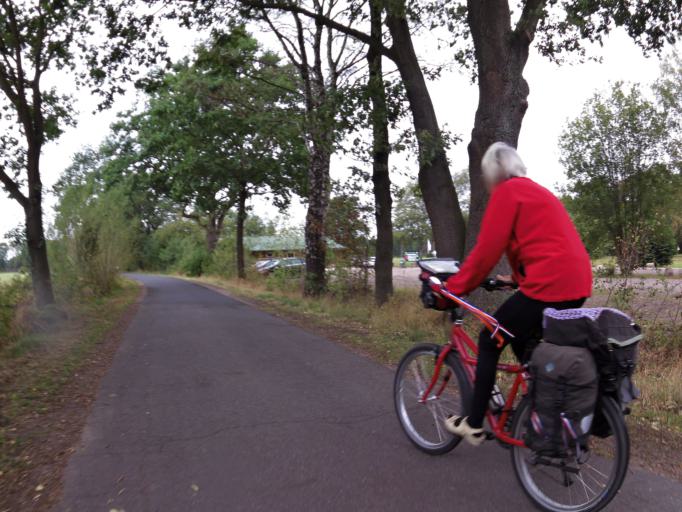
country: DE
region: Lower Saxony
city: Sittensen
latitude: 53.2725
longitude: 9.4922
